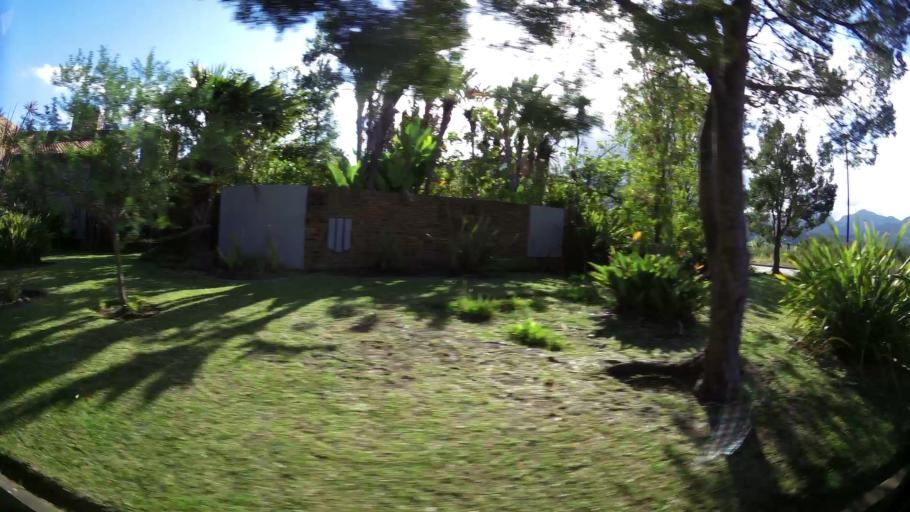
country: ZA
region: Western Cape
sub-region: Eden District Municipality
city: George
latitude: -33.9665
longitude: 22.4967
